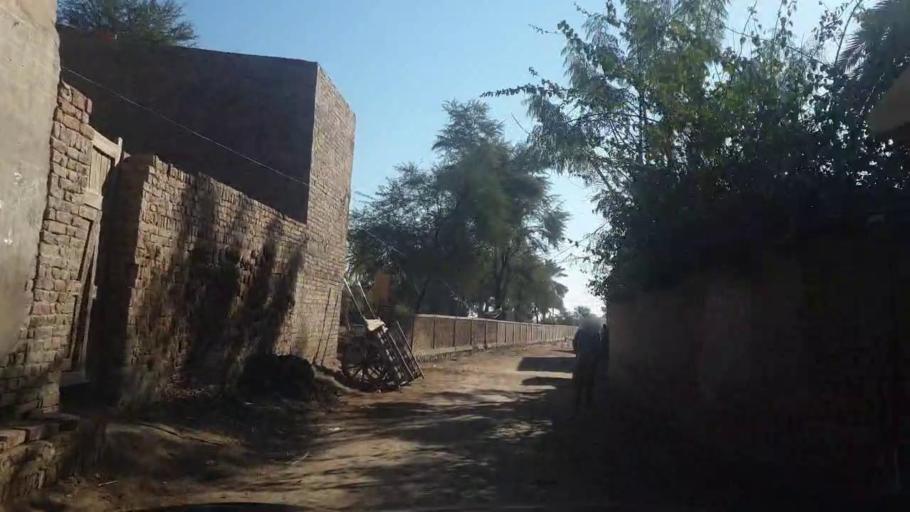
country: PK
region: Sindh
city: Ghotki
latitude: 27.9837
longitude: 69.3250
